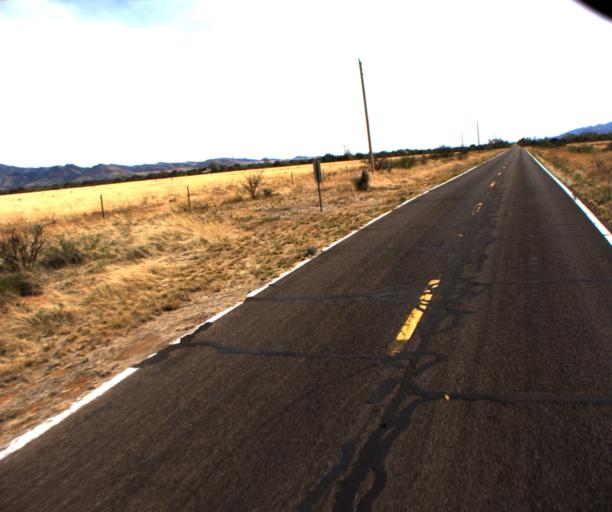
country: US
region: Arizona
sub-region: Cochise County
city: Willcox
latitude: 31.8972
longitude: -109.4914
